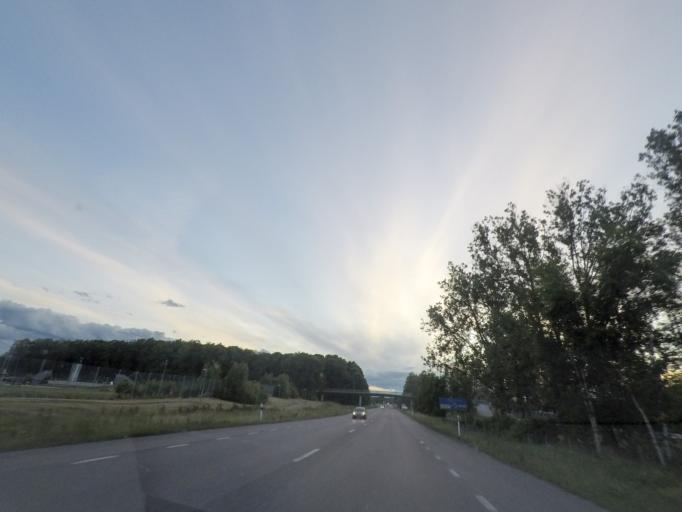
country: SE
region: Stockholm
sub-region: Sigtuna Kommun
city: Marsta
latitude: 59.6246
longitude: 17.8298
